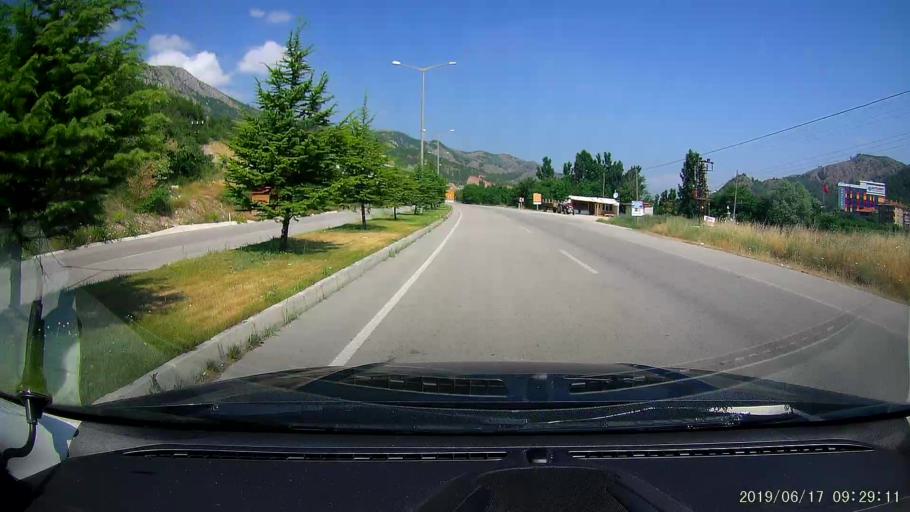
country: TR
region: Amasya
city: Amasya
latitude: 40.6948
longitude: 35.8152
